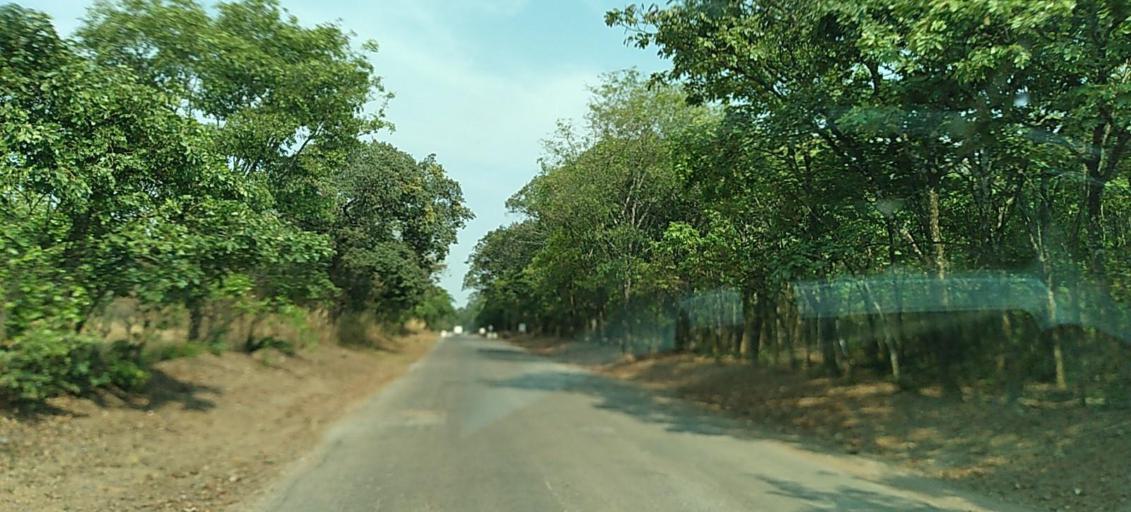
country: ZM
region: Copperbelt
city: Chililabombwe
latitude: -12.3046
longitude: 27.7834
